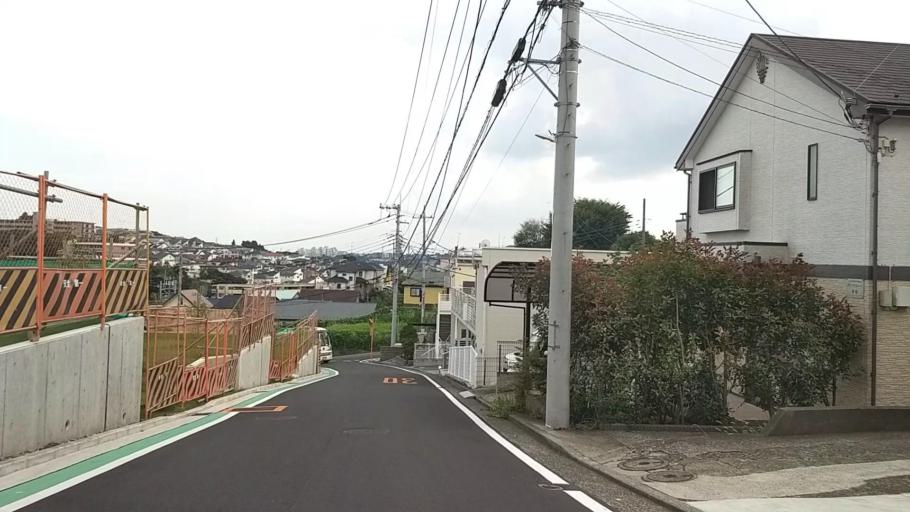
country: JP
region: Kanagawa
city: Yokohama
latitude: 35.4823
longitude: 139.5687
